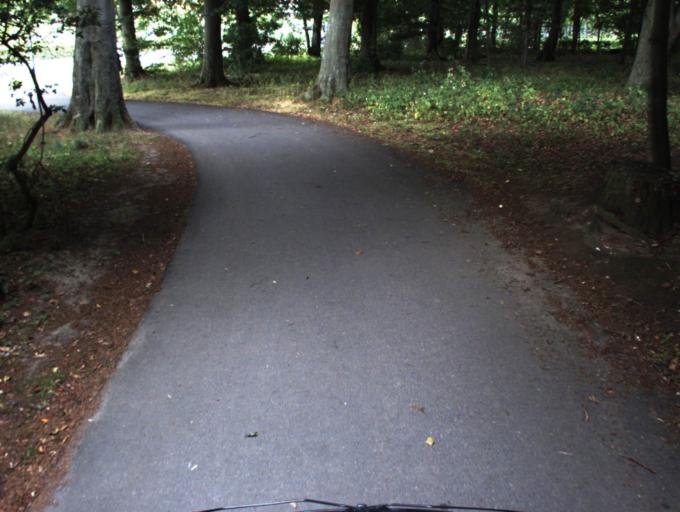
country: SE
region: Skane
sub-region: Helsingborg
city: Helsingborg
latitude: 56.0565
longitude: 12.7077
